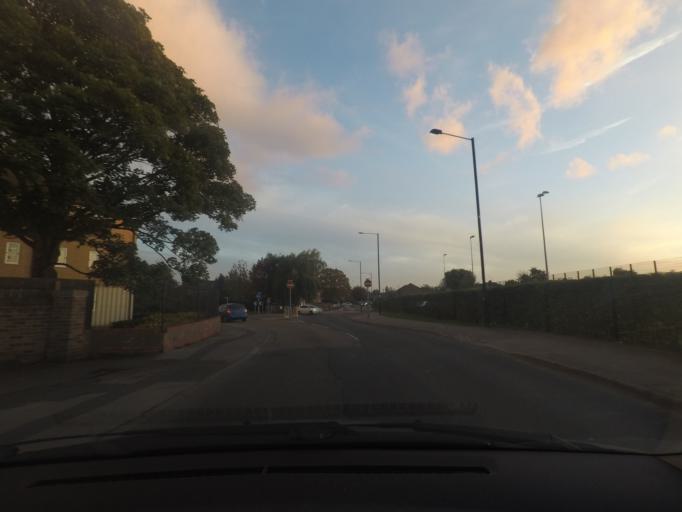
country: GB
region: England
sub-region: City of York
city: York
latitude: 53.9764
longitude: -1.0972
